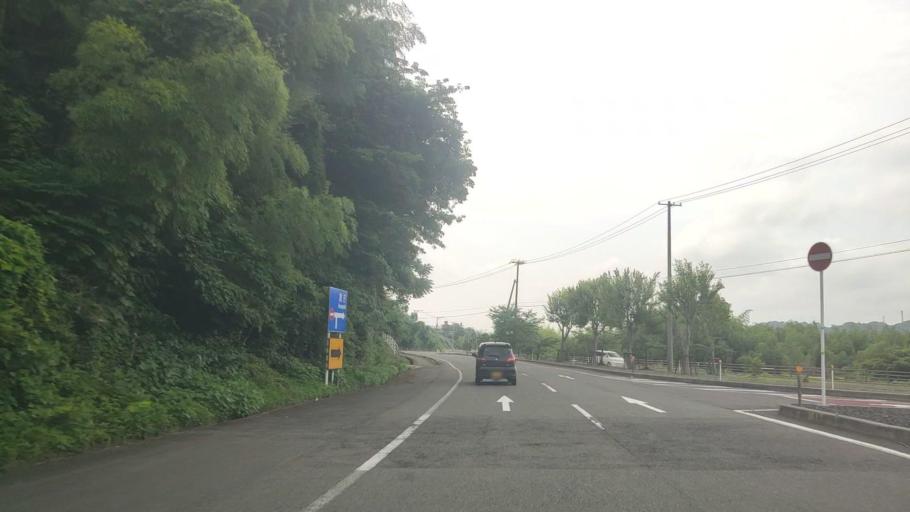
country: JP
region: Tottori
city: Kurayoshi
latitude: 35.4181
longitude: 133.8511
